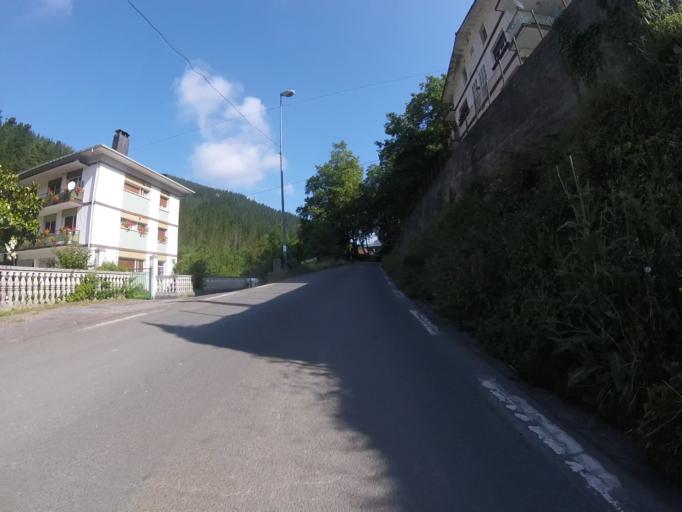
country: ES
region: Basque Country
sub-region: Provincia de Guipuzcoa
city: Ormaiztegui
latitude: 43.0609
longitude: -2.2382
